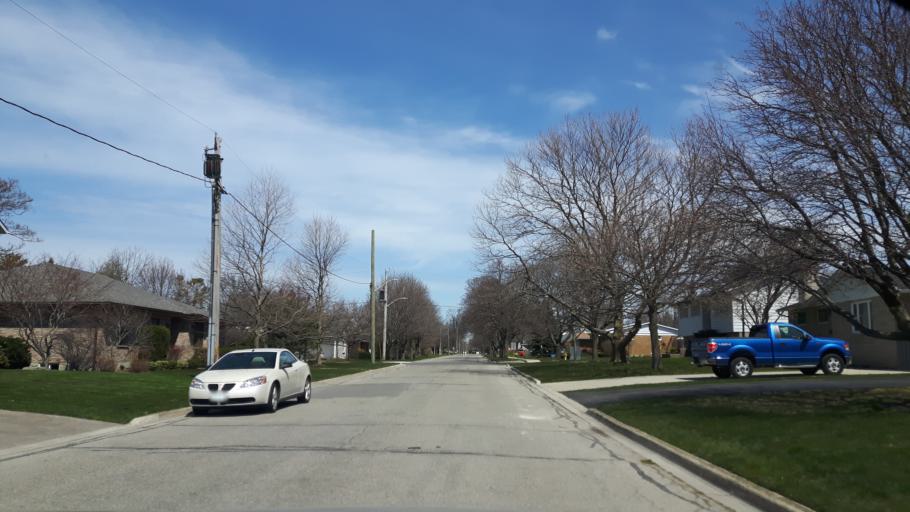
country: CA
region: Ontario
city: Goderich
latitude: 43.7328
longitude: -81.7215
